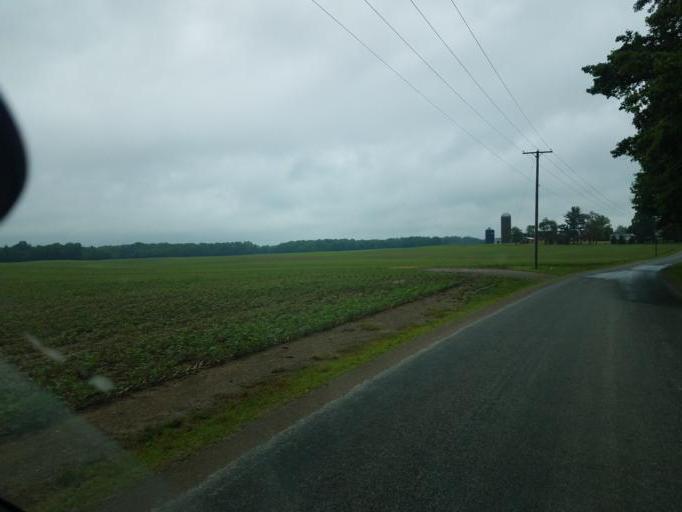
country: US
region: Ohio
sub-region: Richland County
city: Lexington
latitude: 40.5869
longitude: -82.6530
